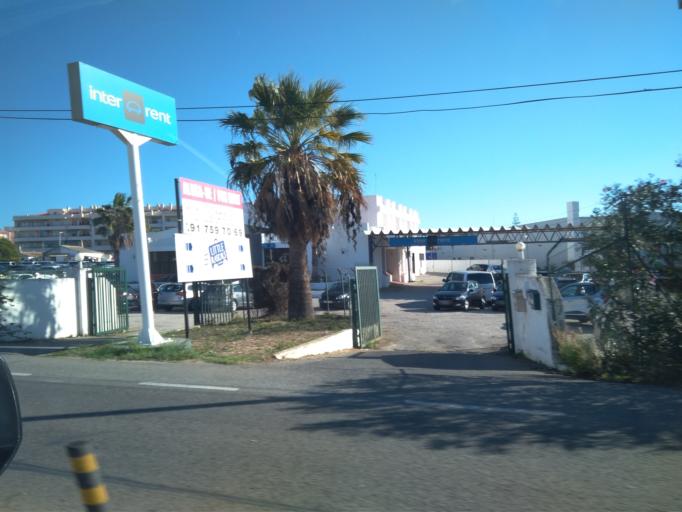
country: PT
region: Faro
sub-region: Faro
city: Faro
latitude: 37.0280
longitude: -7.9691
